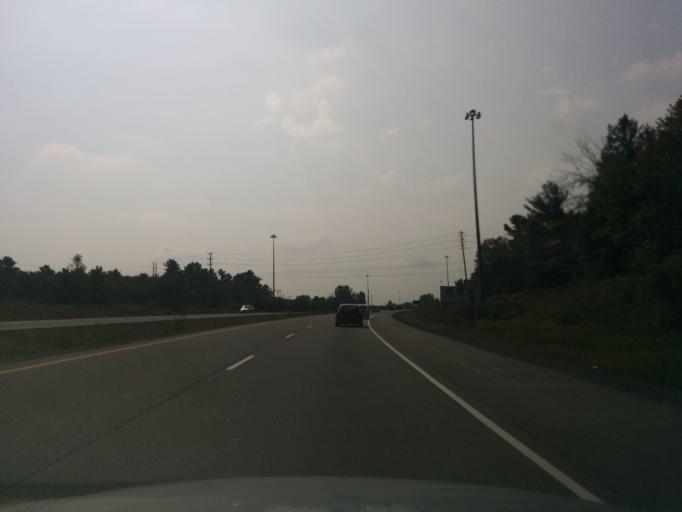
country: CA
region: Ontario
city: Bells Corners
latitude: 45.3249
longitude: -75.8061
